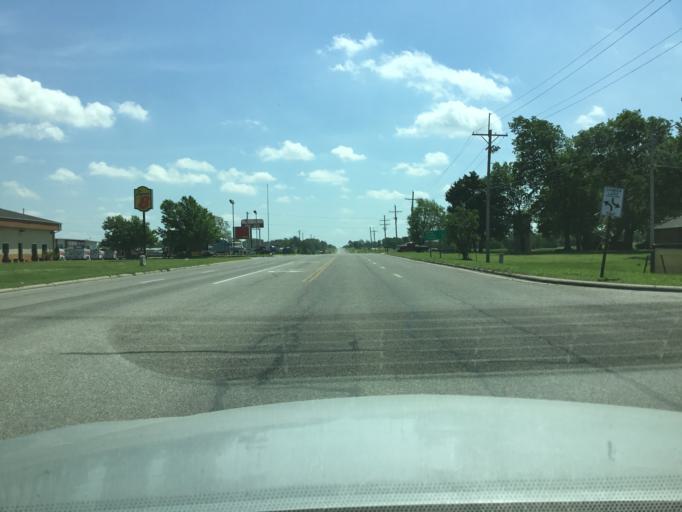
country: US
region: Kansas
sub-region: Labette County
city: Parsons
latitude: 37.3403
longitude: -95.2366
